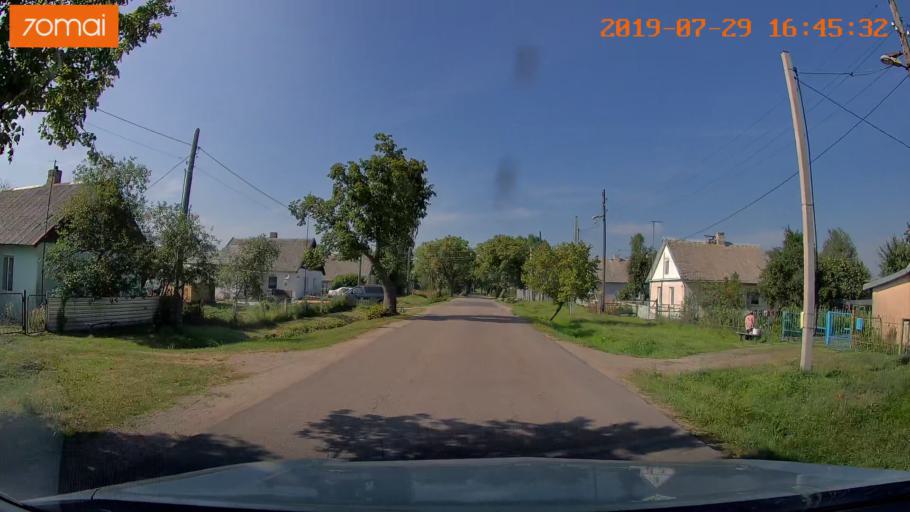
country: RU
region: Kaliningrad
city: Primorsk
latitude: 54.7657
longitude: 20.0802
